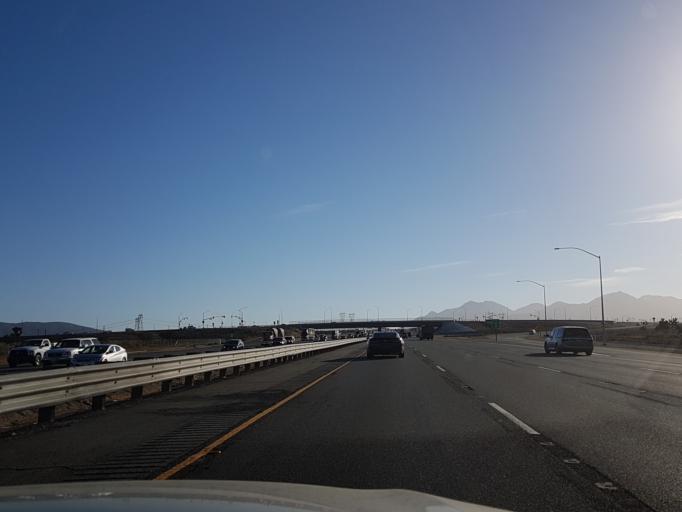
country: US
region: California
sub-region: San Bernardino County
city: Oak Hills
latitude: 34.3870
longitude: -117.4123
